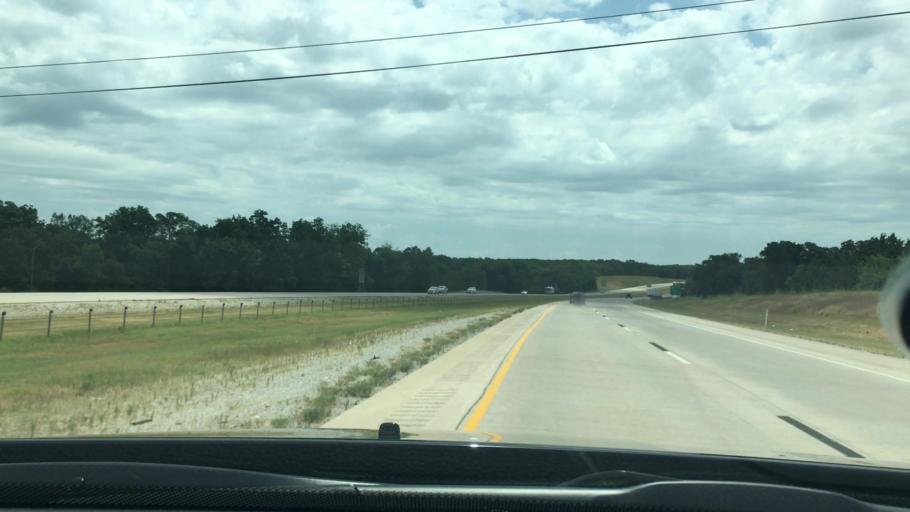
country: US
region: Oklahoma
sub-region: Carter County
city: Ardmore
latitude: 34.1509
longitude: -97.1578
